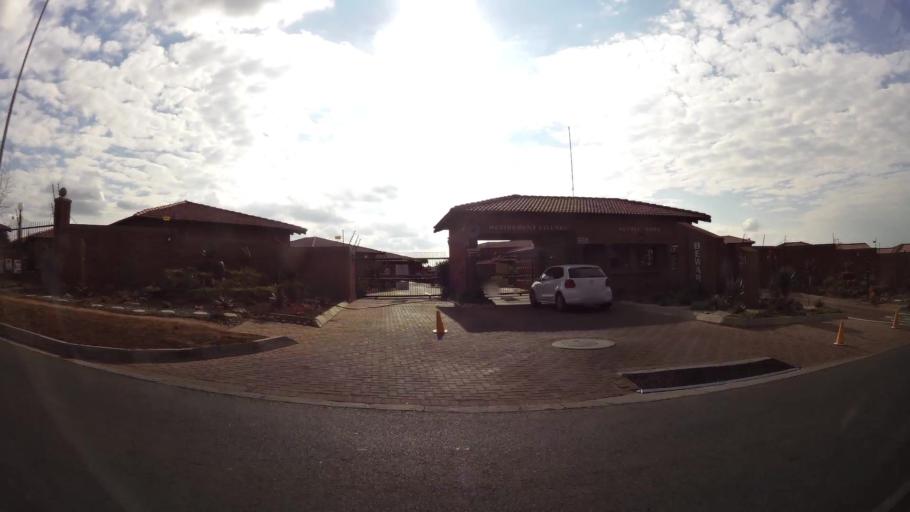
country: ZA
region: Orange Free State
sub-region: Mangaung Metropolitan Municipality
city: Bloemfontein
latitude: -29.0765
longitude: 26.2167
